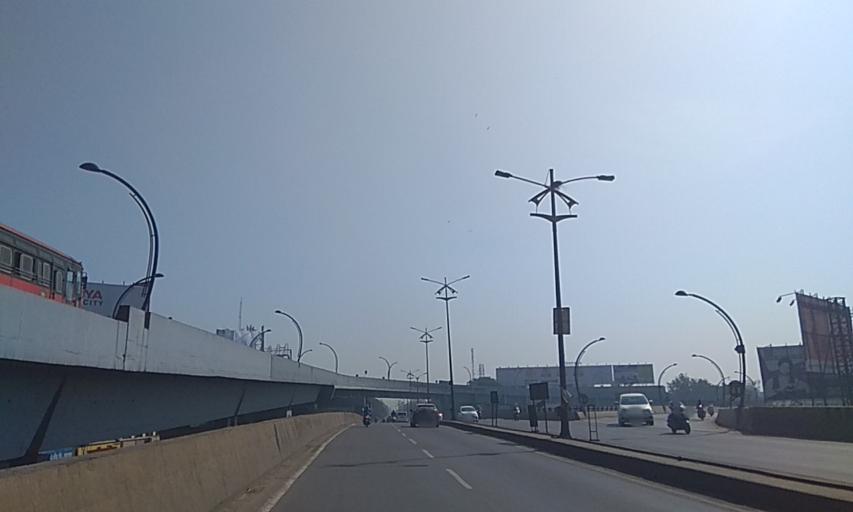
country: IN
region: Maharashtra
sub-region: Pune Division
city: Pune
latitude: 18.5010
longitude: 73.9378
